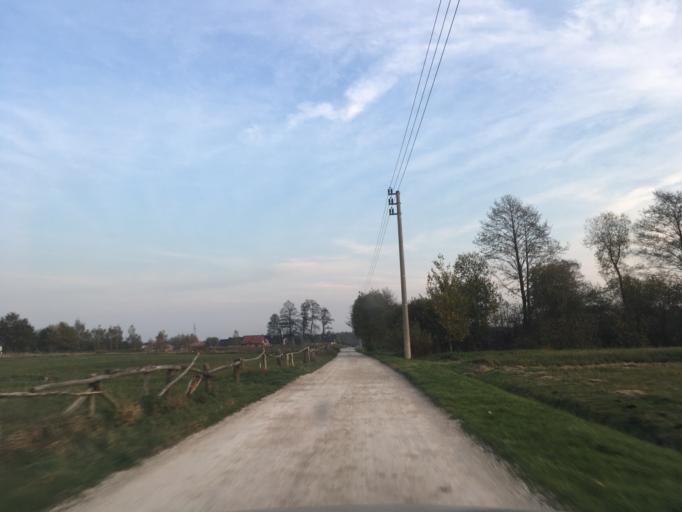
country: PL
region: Masovian Voivodeship
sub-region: Powiat piaseczynski
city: Lesznowola
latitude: 52.0507
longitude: 20.9255
